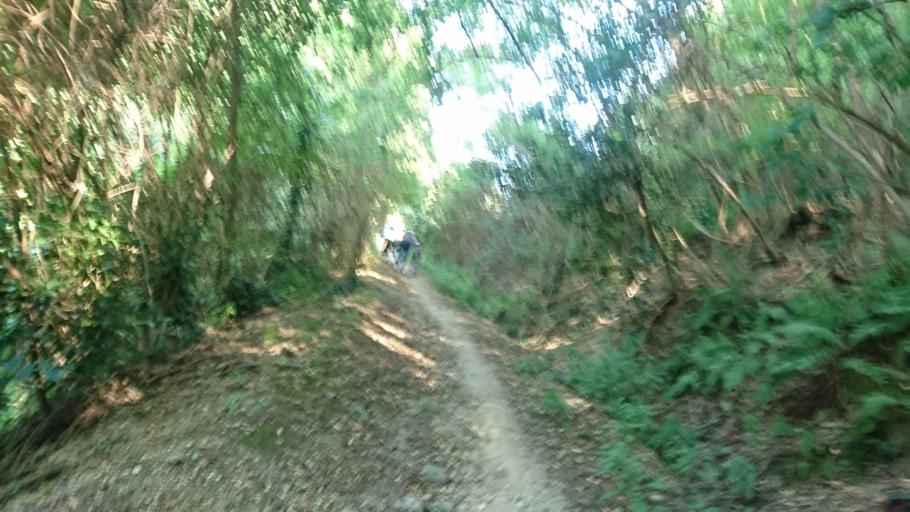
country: IT
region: Veneto
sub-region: Provincia di Padova
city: Galzignano
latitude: 45.3132
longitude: 11.7490
